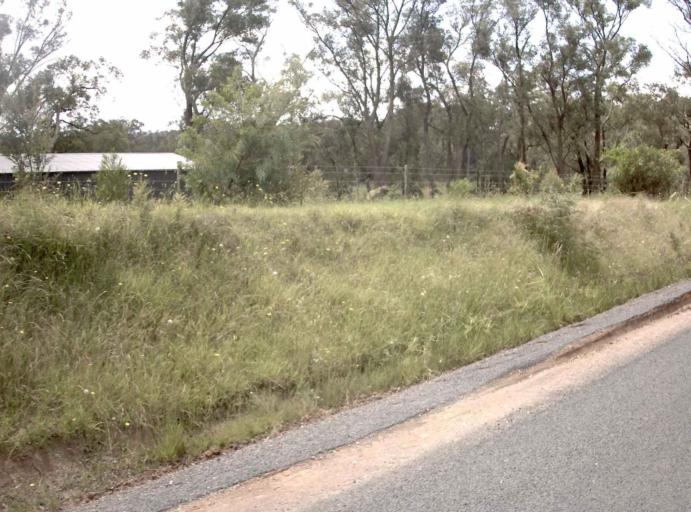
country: AU
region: Victoria
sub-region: Baw Baw
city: Warragul
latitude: -38.0796
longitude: 145.9221
